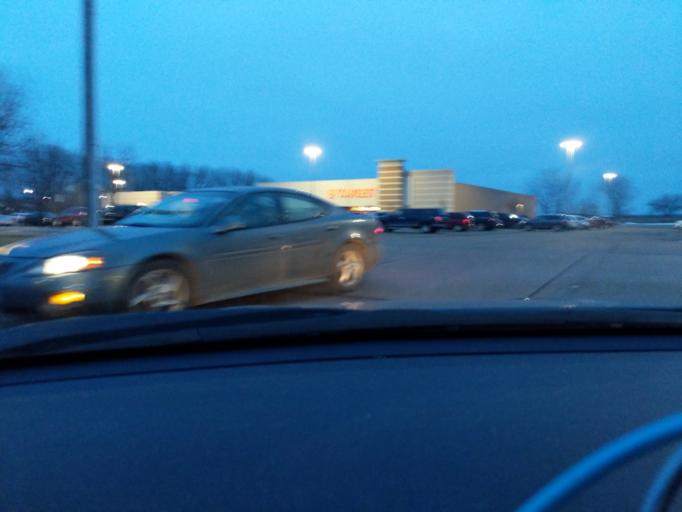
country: US
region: Minnesota
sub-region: Kandiyohi County
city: Willmar
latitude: 45.0974
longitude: -95.0425
